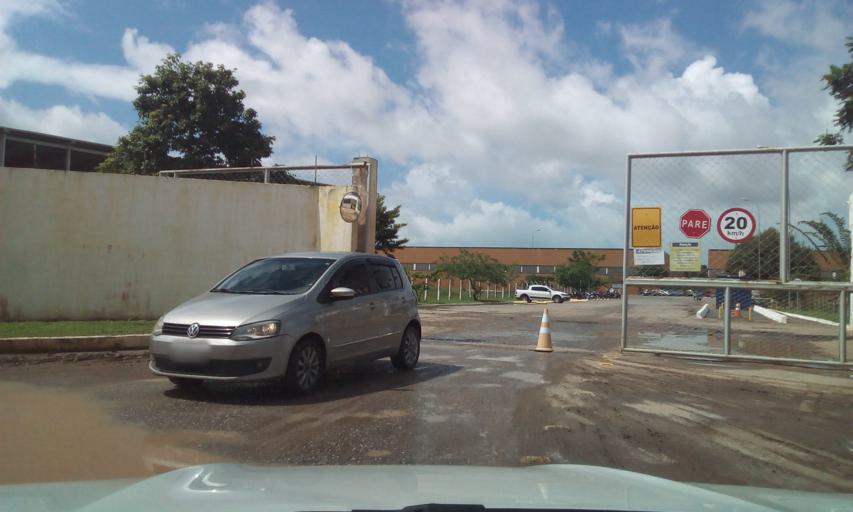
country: BR
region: Paraiba
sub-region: Conde
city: Conde
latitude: -7.1931
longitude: -34.8978
